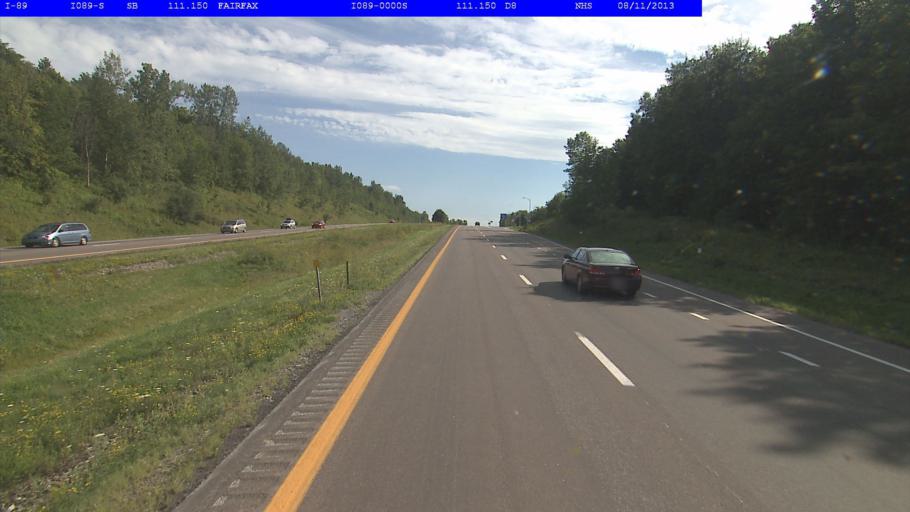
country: US
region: Vermont
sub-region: Franklin County
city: Saint Albans
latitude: 44.7578
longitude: -73.0771
